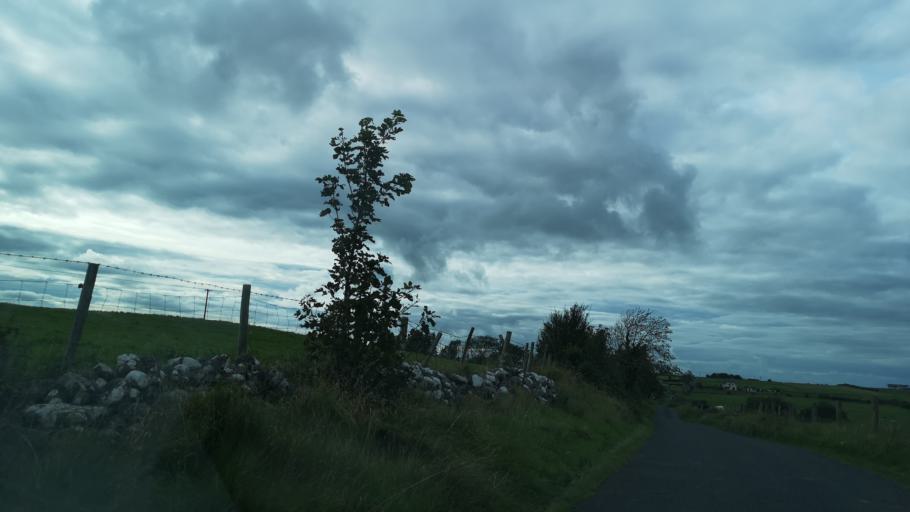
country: IE
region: Connaught
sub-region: County Galway
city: Ballinasloe
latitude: 53.3743
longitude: -8.1674
